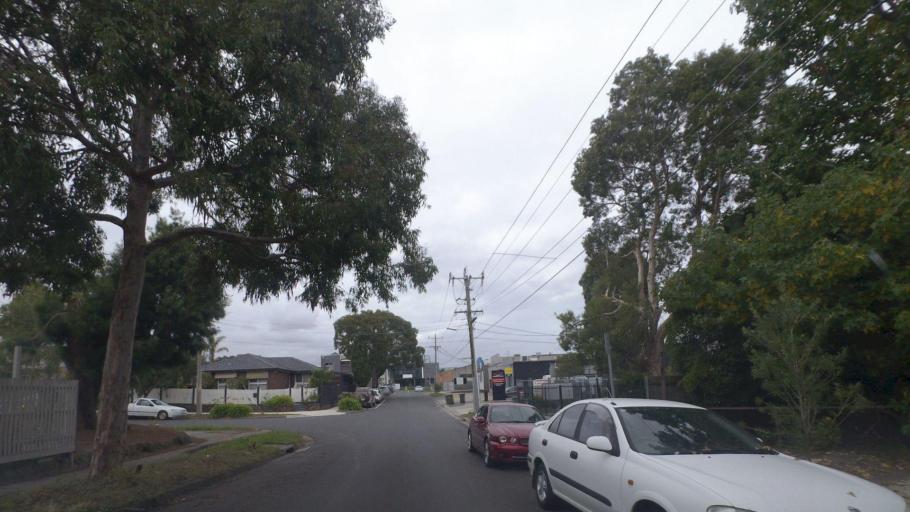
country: AU
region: Victoria
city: Forest Hill
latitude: -37.8306
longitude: 145.1856
